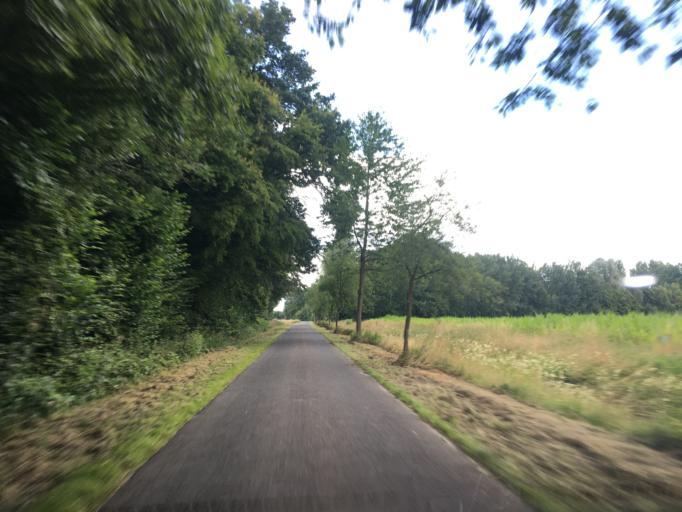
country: DE
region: North Rhine-Westphalia
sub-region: Regierungsbezirk Munster
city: Muenster
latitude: 52.0218
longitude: 7.5911
